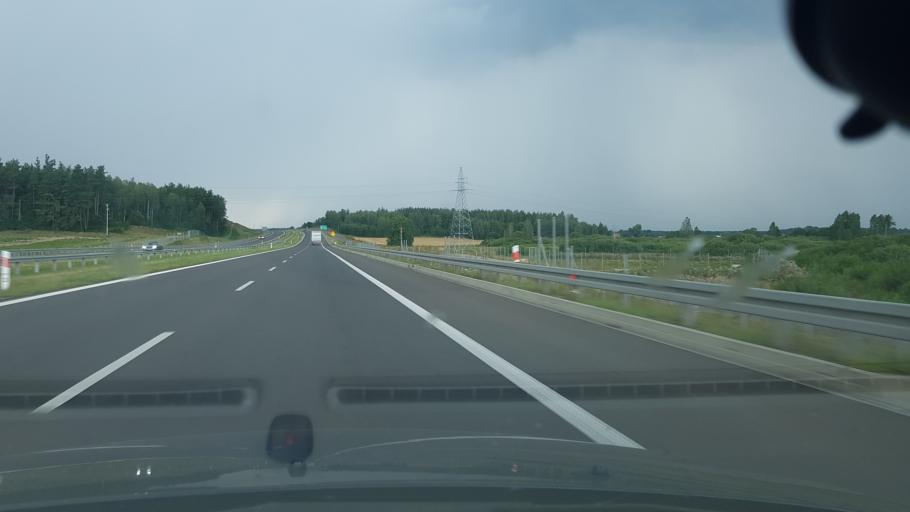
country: PL
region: Warmian-Masurian Voivodeship
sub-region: Powiat nidzicki
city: Nidzica
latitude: 53.3611
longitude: 20.3901
